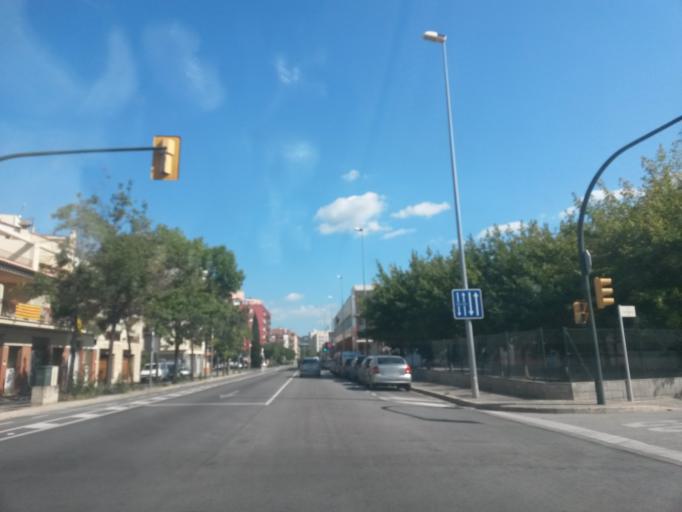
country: ES
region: Catalonia
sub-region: Provincia de Girona
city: Salt
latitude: 41.9670
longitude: 2.8099
